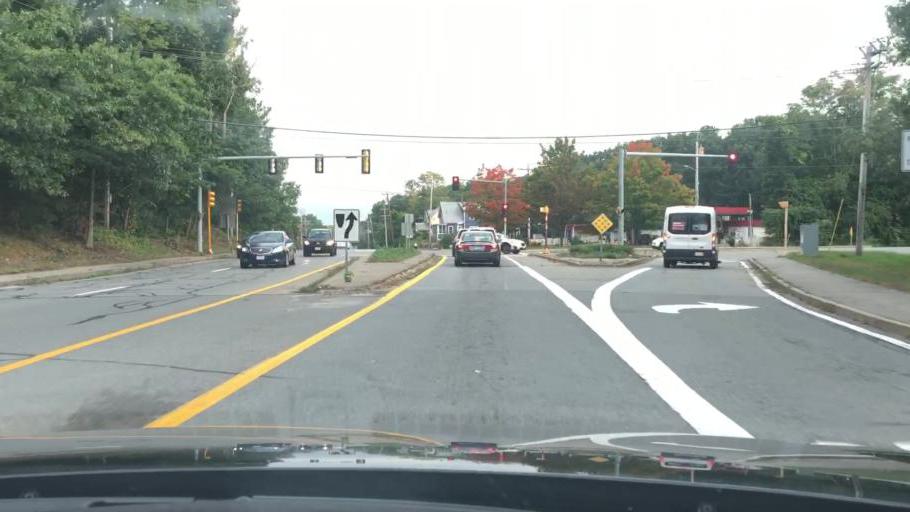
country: US
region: Massachusetts
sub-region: Middlesex County
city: Chelmsford
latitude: 42.6307
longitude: -71.3735
